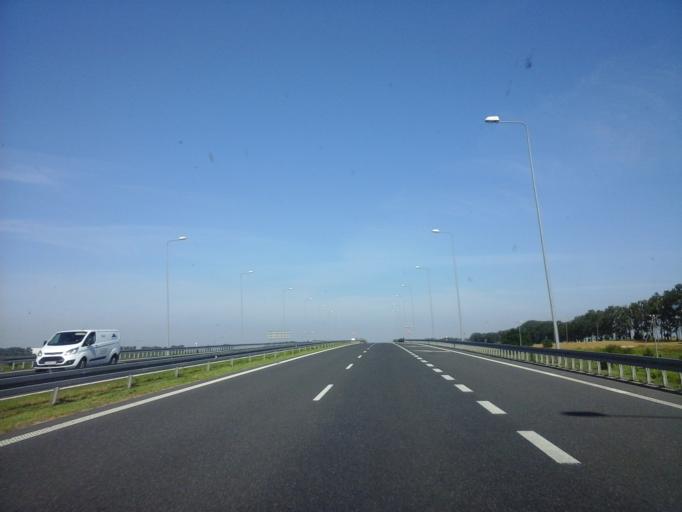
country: PL
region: West Pomeranian Voivodeship
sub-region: Powiat stargardzki
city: Stargard Szczecinski
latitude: 53.3072
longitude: 15.0241
